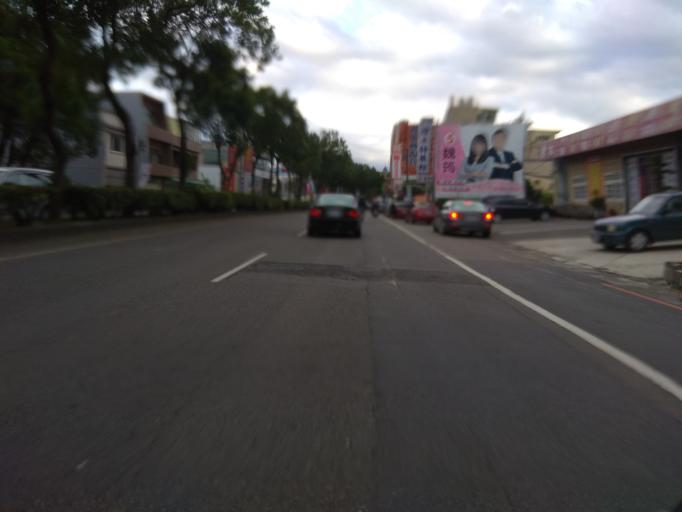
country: TW
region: Taiwan
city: Daxi
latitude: 24.8769
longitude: 121.2124
